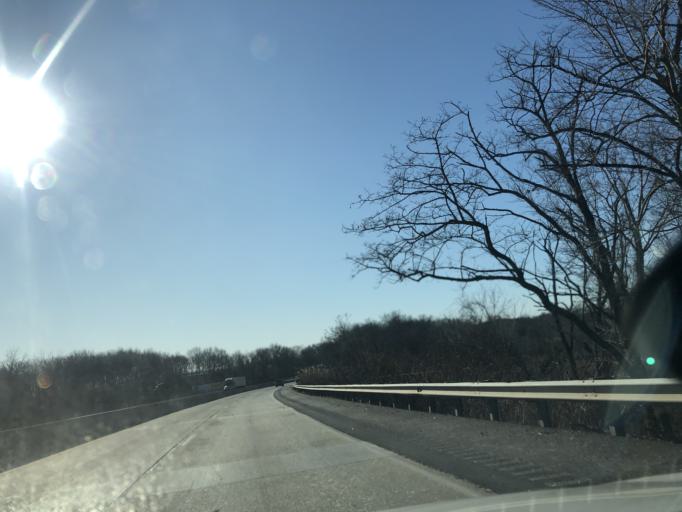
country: US
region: Pennsylvania
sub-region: Bucks County
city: Morrisville
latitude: 40.1916
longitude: -74.8010
